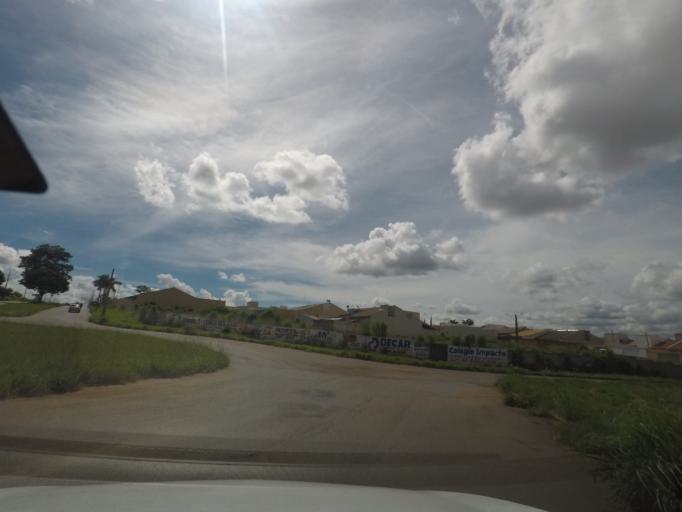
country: BR
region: Goias
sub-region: Goiania
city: Goiania
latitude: -16.7440
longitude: -49.3374
